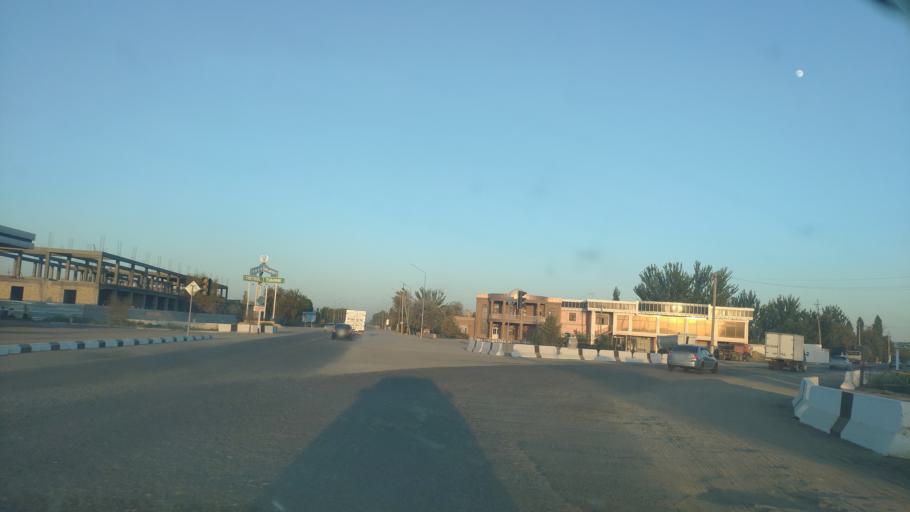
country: UZ
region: Karakalpakstan
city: To'rtko'l Shahri
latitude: 41.5681
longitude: 60.9511
